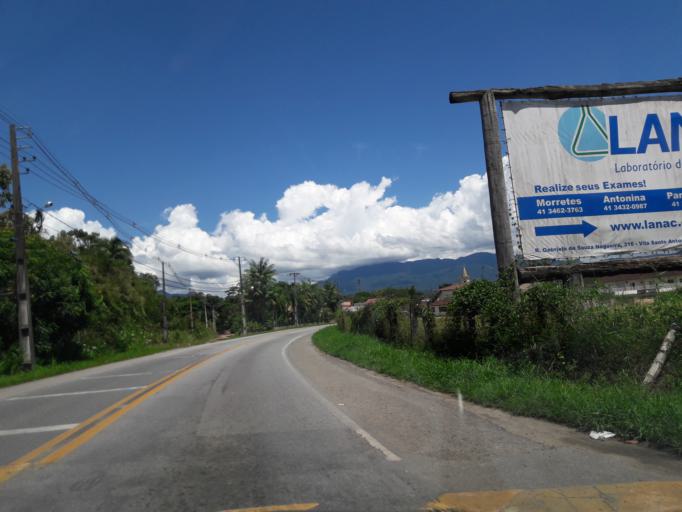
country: BR
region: Parana
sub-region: Antonina
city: Antonina
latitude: -25.4744
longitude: -48.8289
